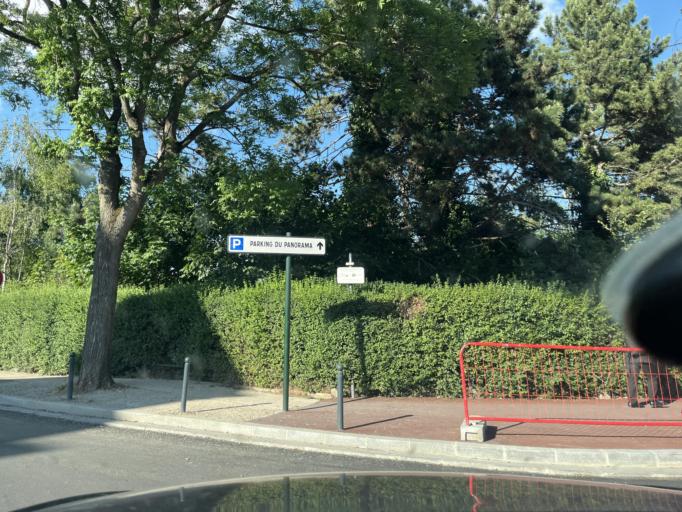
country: FR
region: Ile-de-France
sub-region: Departement des Hauts-de-Seine
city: Le Plessis-Robinson
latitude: 48.7909
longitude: 2.2730
